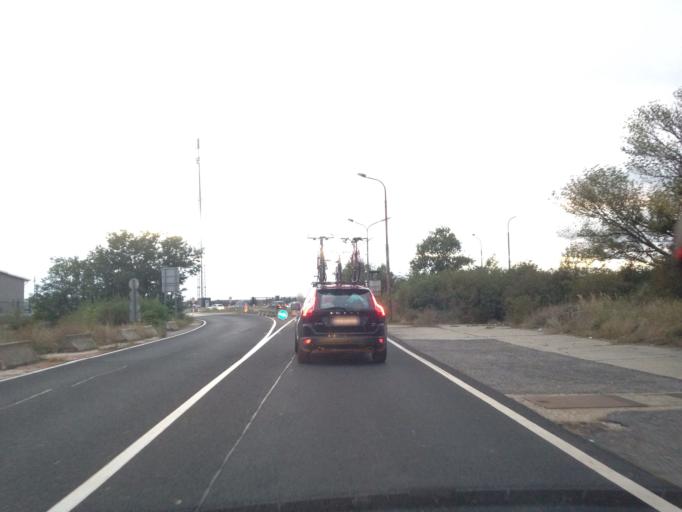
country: AT
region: Burgenland
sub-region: Politischer Bezirk Neusiedl am See
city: Nickelsdorf
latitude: 47.9270
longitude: 17.1137
